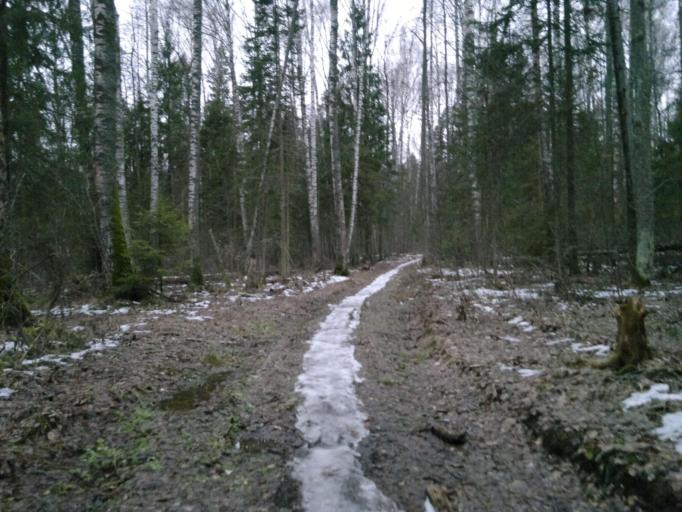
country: RU
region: Mariy-El
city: Yoshkar-Ola
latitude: 56.6048
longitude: 47.9560
